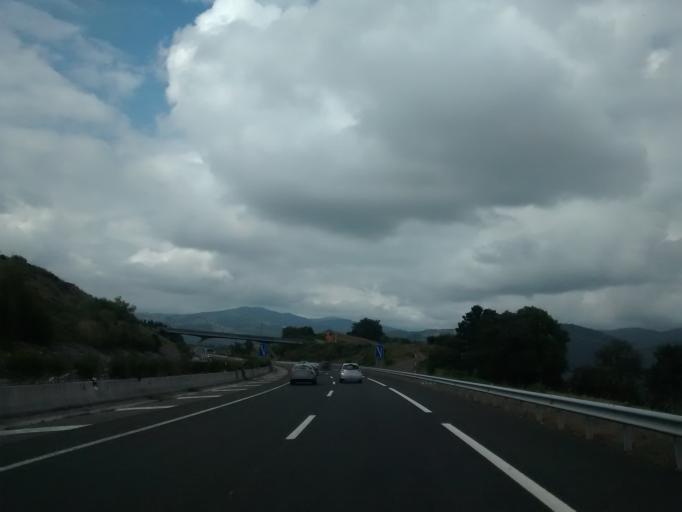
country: ES
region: Cantabria
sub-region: Provincia de Cantabria
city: Barcena de Pie de Concha
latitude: 43.1410
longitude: -4.0565
